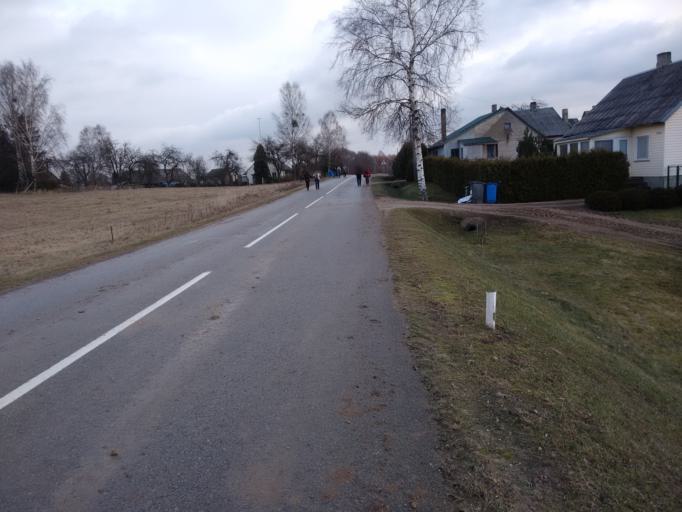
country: LT
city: Veisiejai
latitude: 54.2395
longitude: 23.8332
